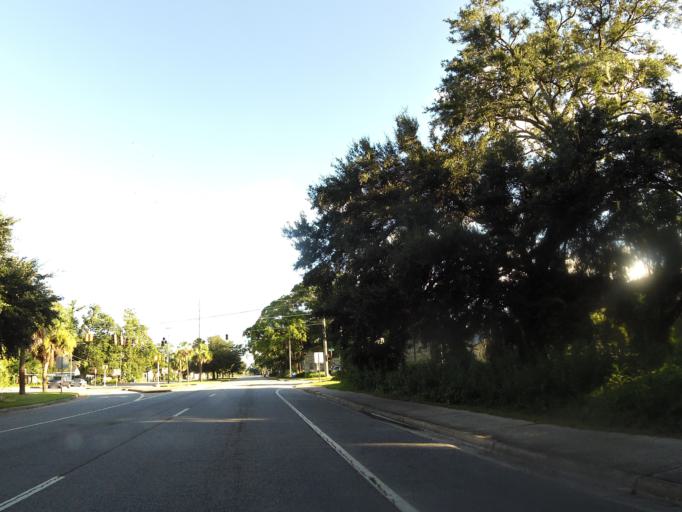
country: US
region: Georgia
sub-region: Glynn County
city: Brunswick
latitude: 31.1544
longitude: -81.4893
